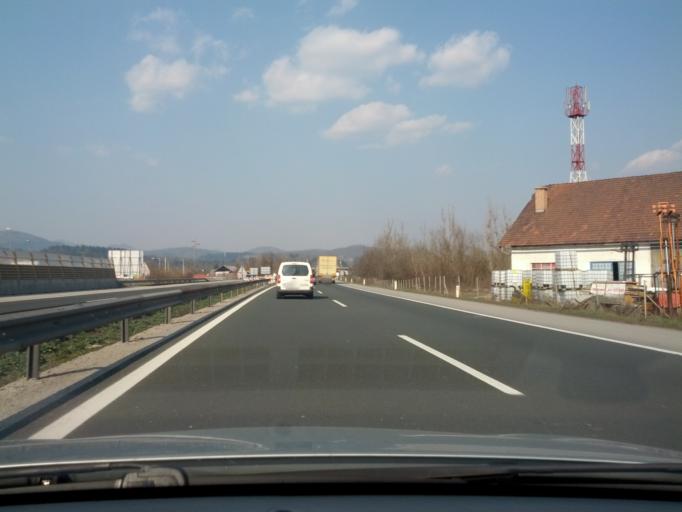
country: SI
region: Vrhnika
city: Vrhnika
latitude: 45.9735
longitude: 14.3068
